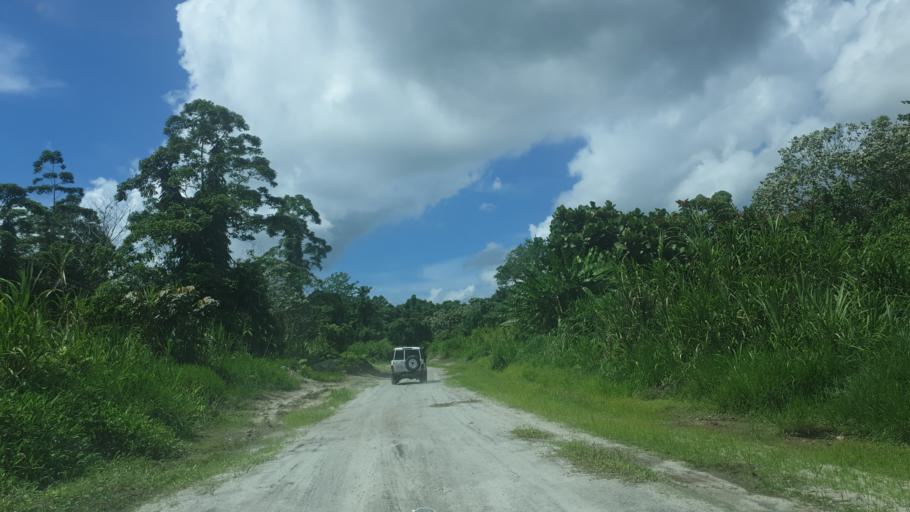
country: PG
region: Bougainville
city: Panguna
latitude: -6.7389
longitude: 155.5021
